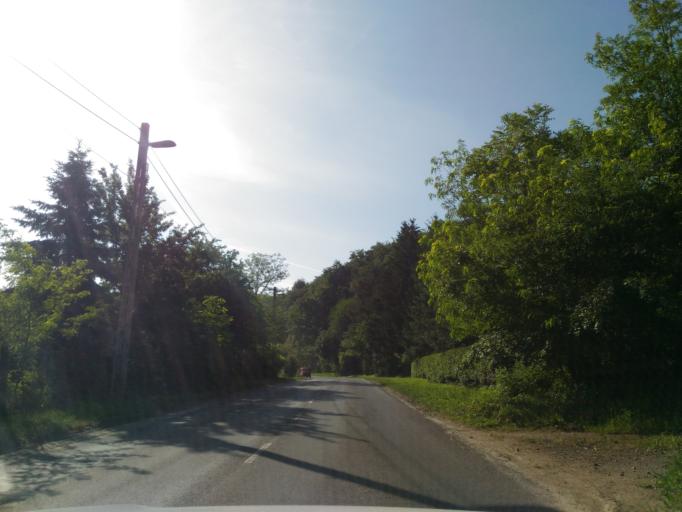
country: HU
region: Baranya
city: Komlo
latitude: 46.1842
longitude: 18.2860
